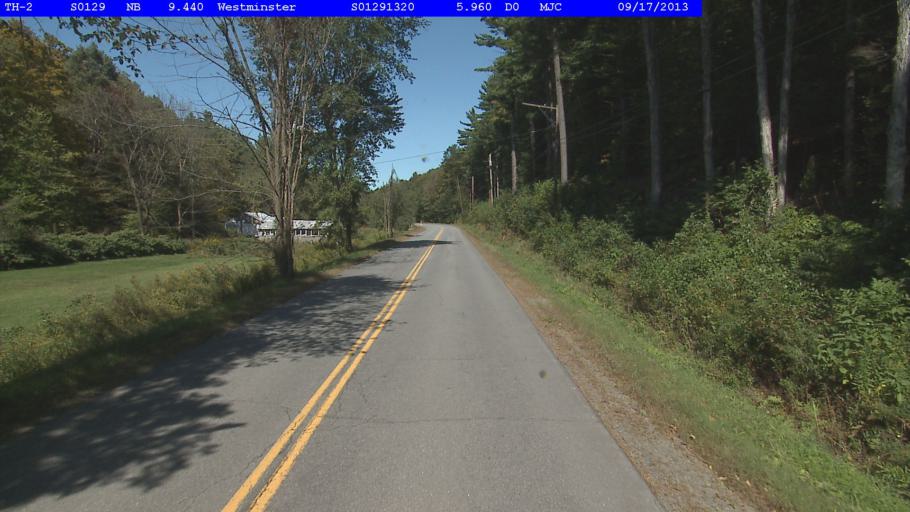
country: US
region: Vermont
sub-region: Windham County
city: Bellows Falls
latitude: 43.1006
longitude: -72.5363
